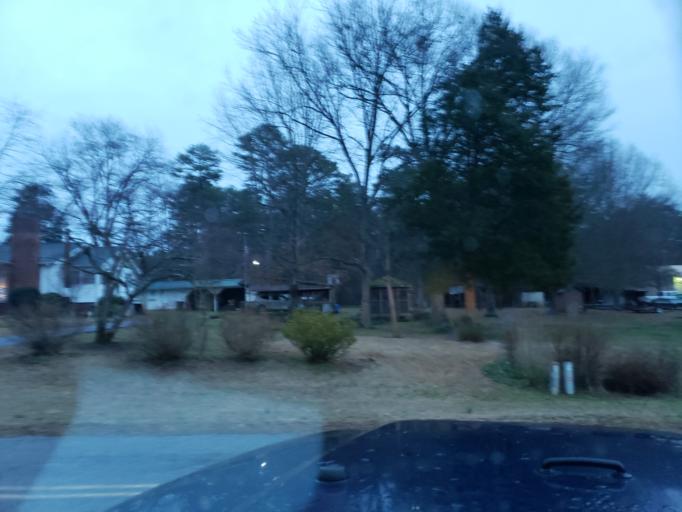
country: US
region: North Carolina
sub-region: Cleveland County
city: White Plains
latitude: 35.1504
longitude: -81.4150
